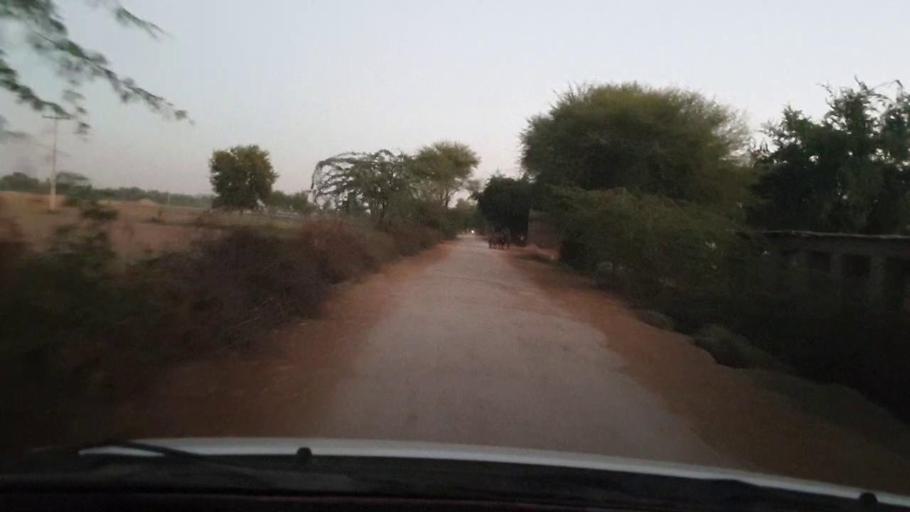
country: PK
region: Sindh
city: Khairpur Nathan Shah
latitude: 27.1349
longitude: 67.7209
